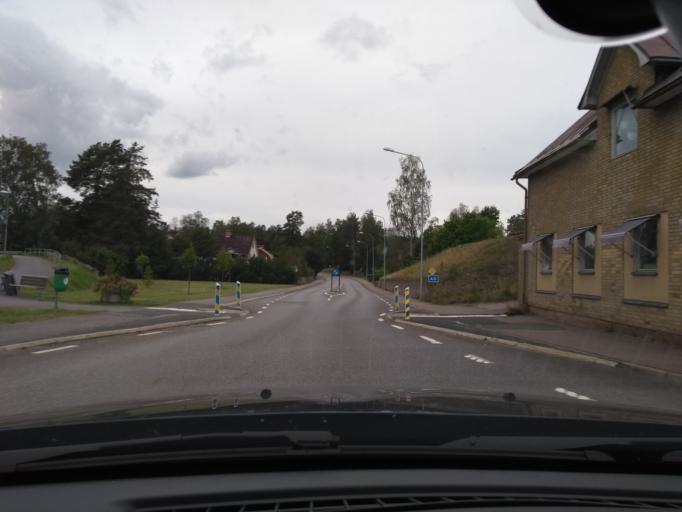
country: SE
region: Joenkoeping
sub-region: Eksjo Kommun
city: Haljarp
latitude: 57.6424
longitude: 15.2740
